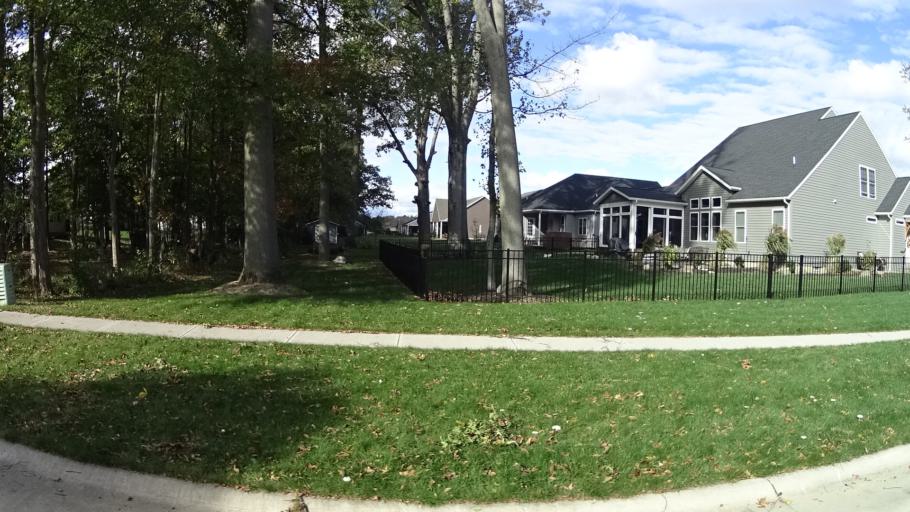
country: US
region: Ohio
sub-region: Lorain County
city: Grafton
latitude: 41.2926
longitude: -82.0601
